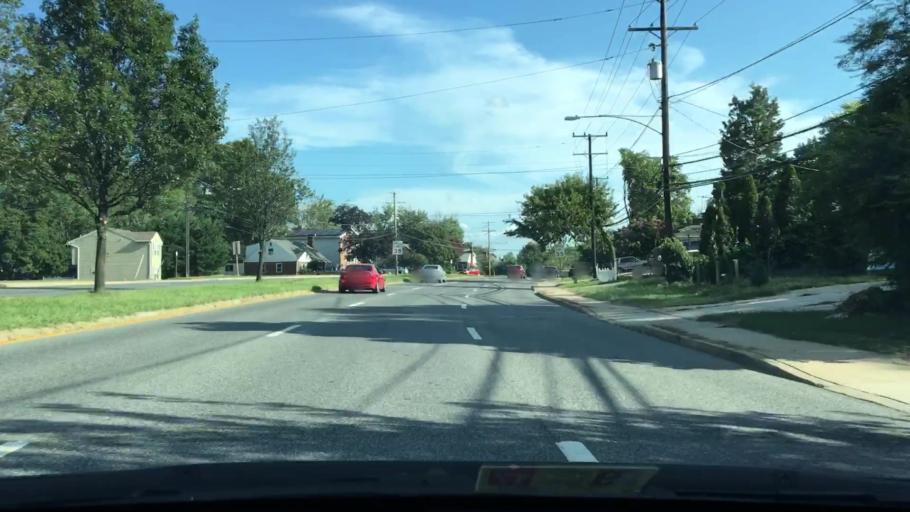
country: US
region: Maryland
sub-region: Montgomery County
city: Kemp Mill
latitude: 39.0294
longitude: -77.0210
